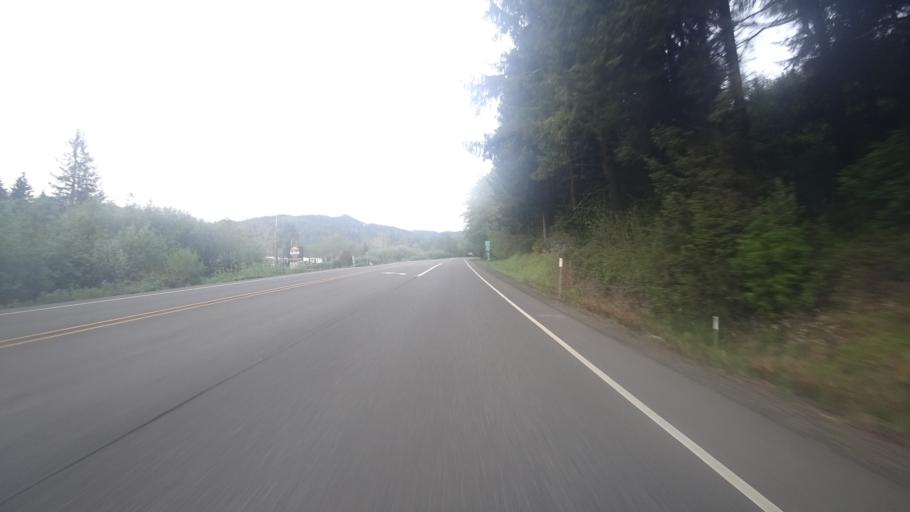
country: US
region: Oregon
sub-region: Douglas County
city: Reedsport
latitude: 43.6760
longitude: -124.1589
